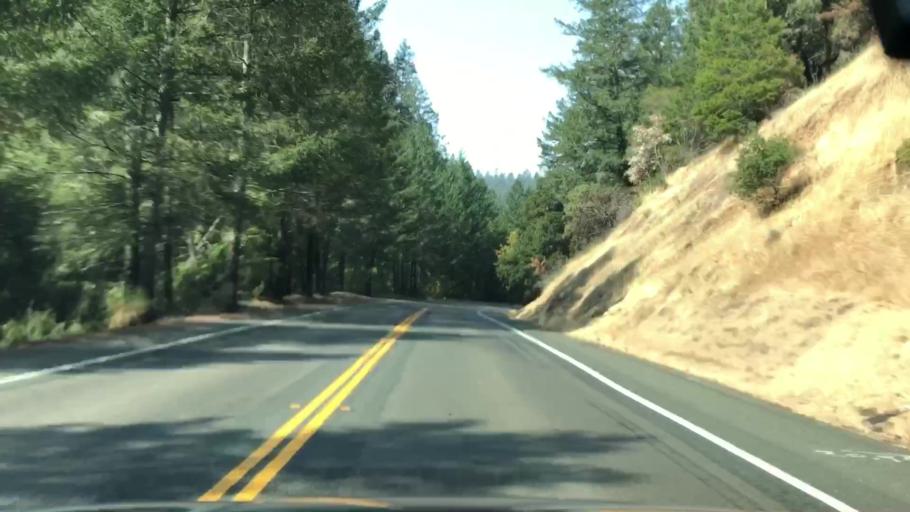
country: US
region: California
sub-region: Napa County
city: Calistoga
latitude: 38.5538
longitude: -122.6441
